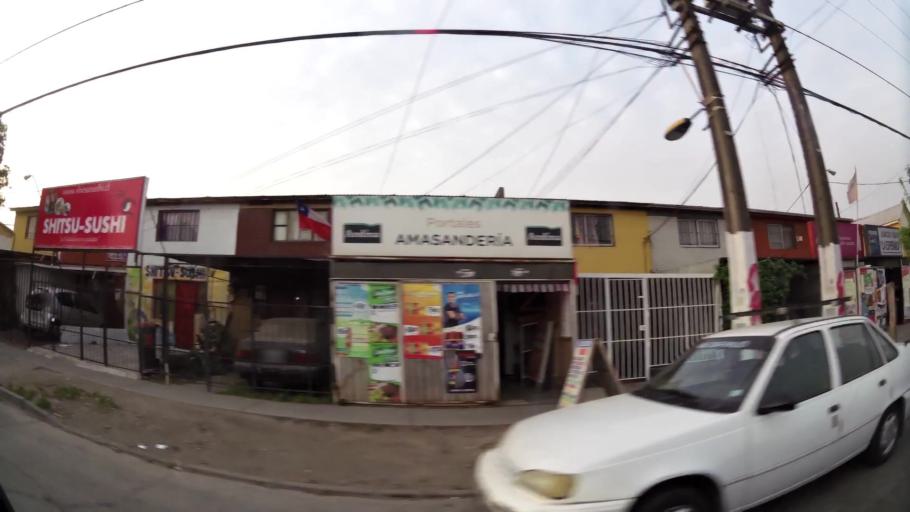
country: CL
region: Santiago Metropolitan
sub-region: Provincia de Santiago
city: Lo Prado
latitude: -33.5183
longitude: -70.7850
